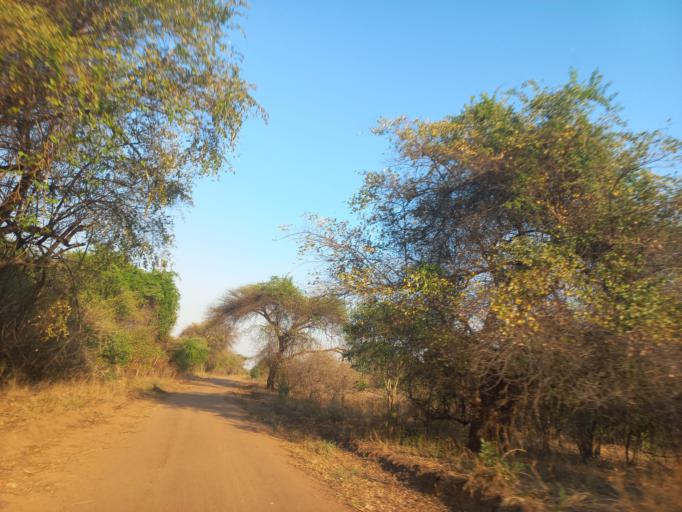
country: ZM
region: Lusaka
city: Luangwa
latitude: -15.4291
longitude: 30.3363
